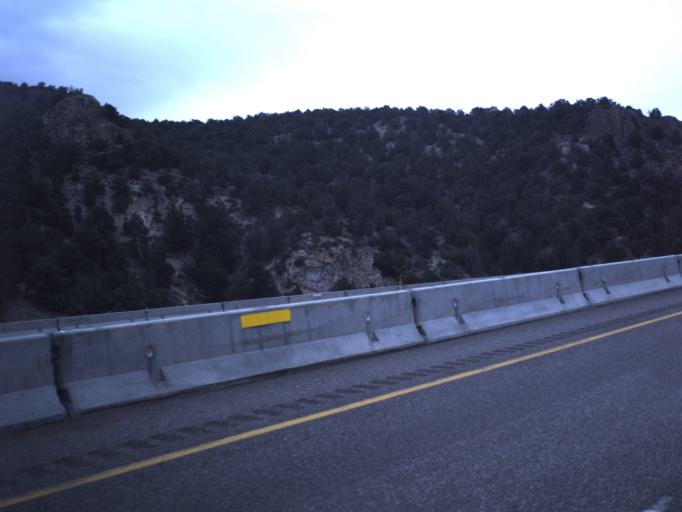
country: US
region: Utah
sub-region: Sevier County
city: Monroe
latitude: 38.5623
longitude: -112.4285
